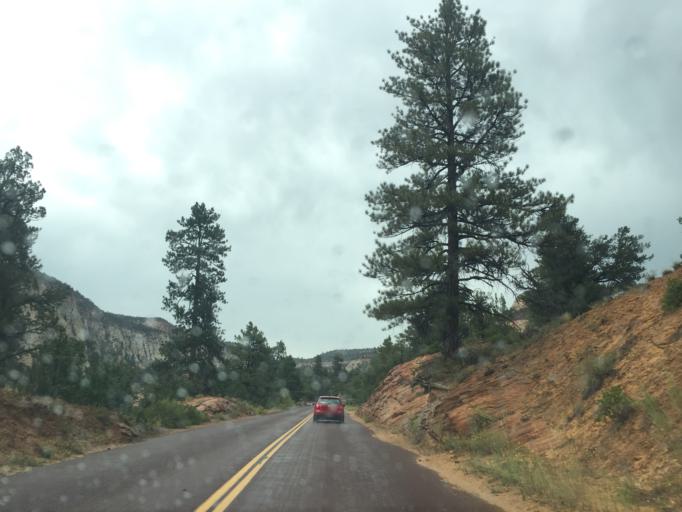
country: US
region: Utah
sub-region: Washington County
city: Hildale
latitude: 37.2285
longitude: -112.8789
